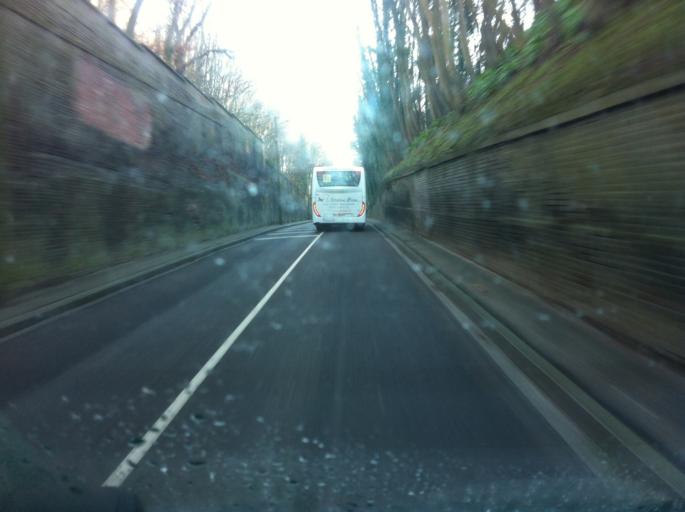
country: FR
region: Haute-Normandie
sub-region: Departement de la Seine-Maritime
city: Eu
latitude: 50.0491
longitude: 1.4068
